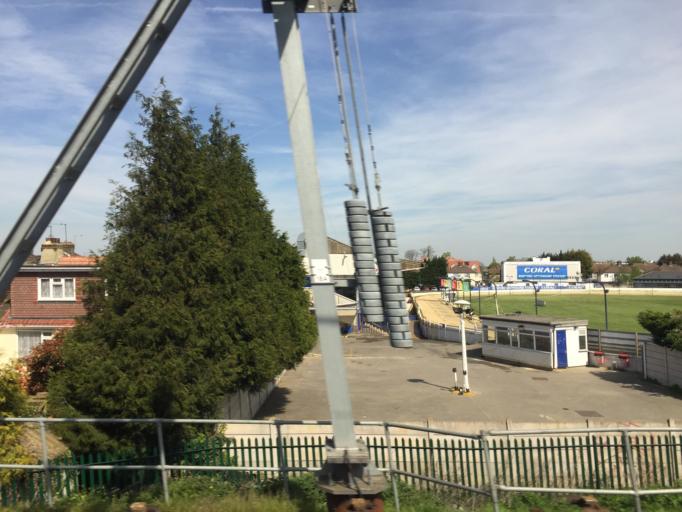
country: GB
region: England
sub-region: Greater London
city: Romford
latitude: 51.5714
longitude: 0.1658
